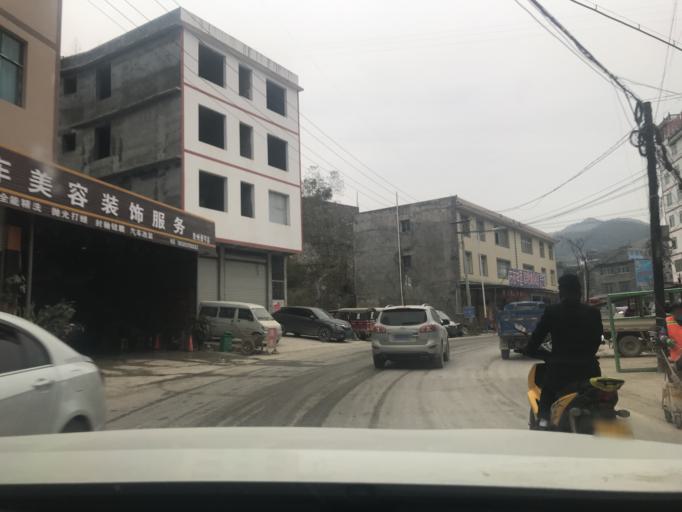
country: CN
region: Guangxi Zhuangzu Zizhiqu
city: Xinzhou
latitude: 24.9816
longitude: 105.8182
